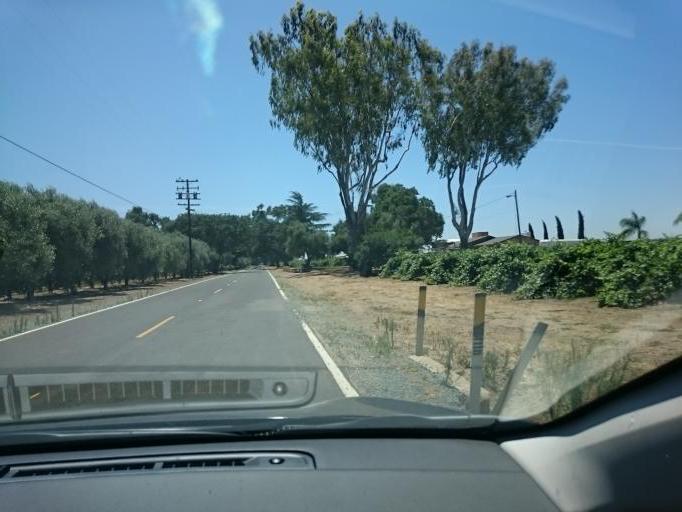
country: US
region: California
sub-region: San Joaquin County
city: Thornton
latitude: 38.1995
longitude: -121.3726
